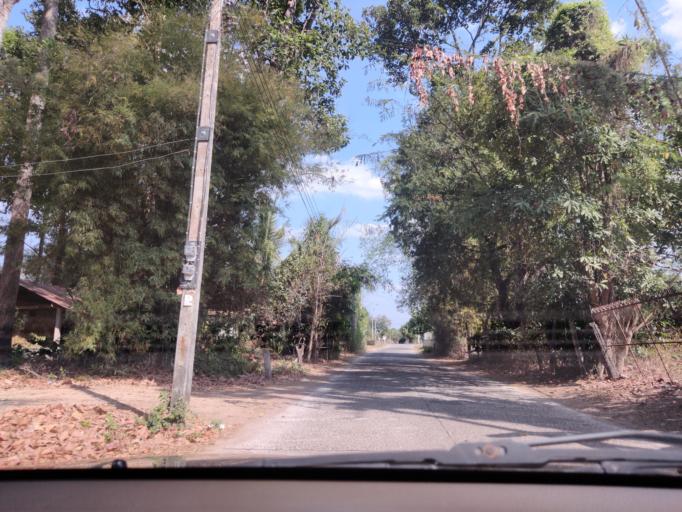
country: TH
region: Sisaket
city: Si Sa Ket
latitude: 15.0655
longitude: 104.3531
